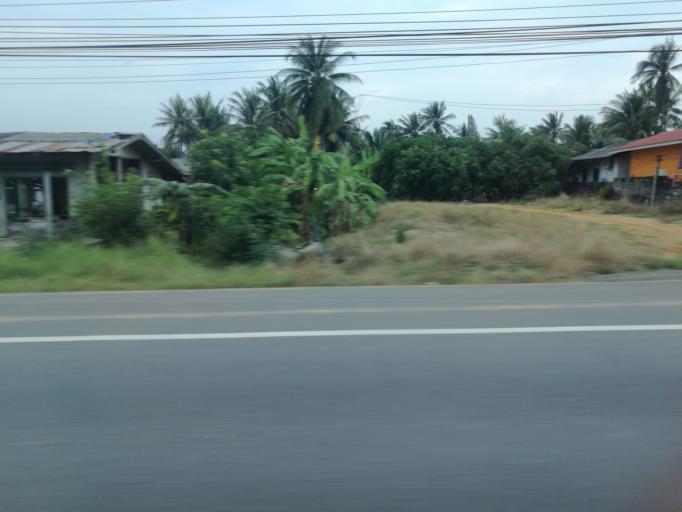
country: TH
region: Prachuap Khiri Khan
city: Sam Roi Yot
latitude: 12.3146
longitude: 99.8775
